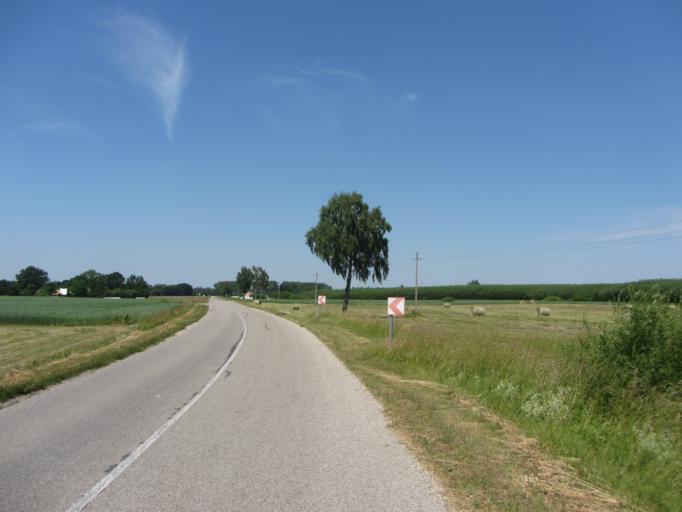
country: LT
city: Sirvintos
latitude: 55.1990
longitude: 24.9532
